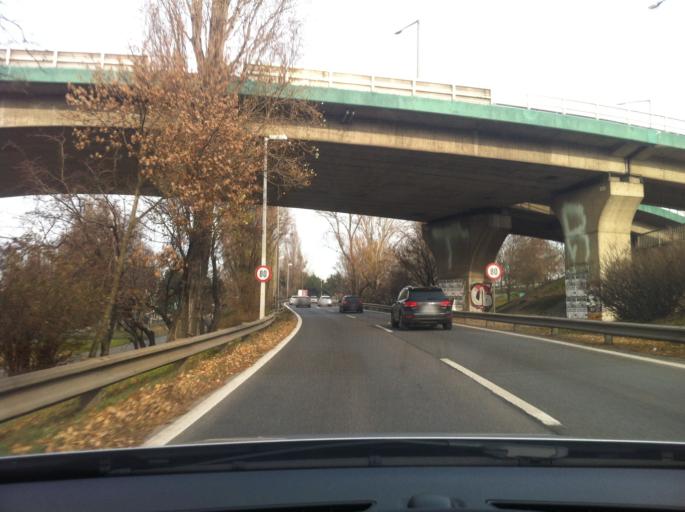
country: AT
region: Vienna
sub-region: Wien Stadt
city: Vienna
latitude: 48.2500
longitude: 16.3729
